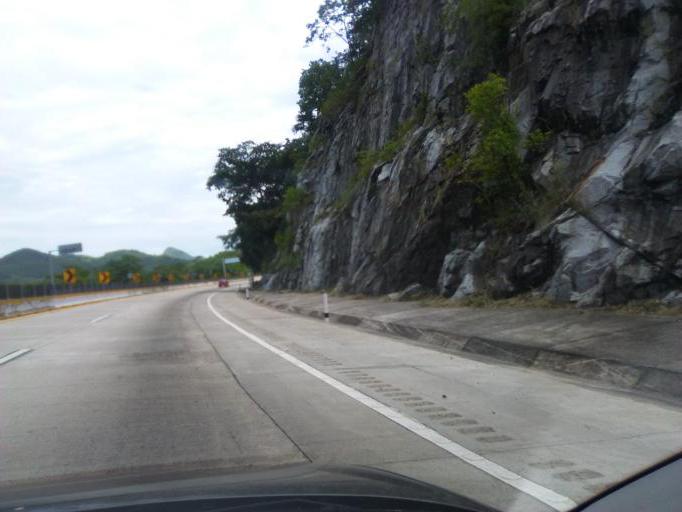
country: MX
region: Guerrero
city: Tierra Colorada
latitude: 17.1868
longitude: -99.5498
